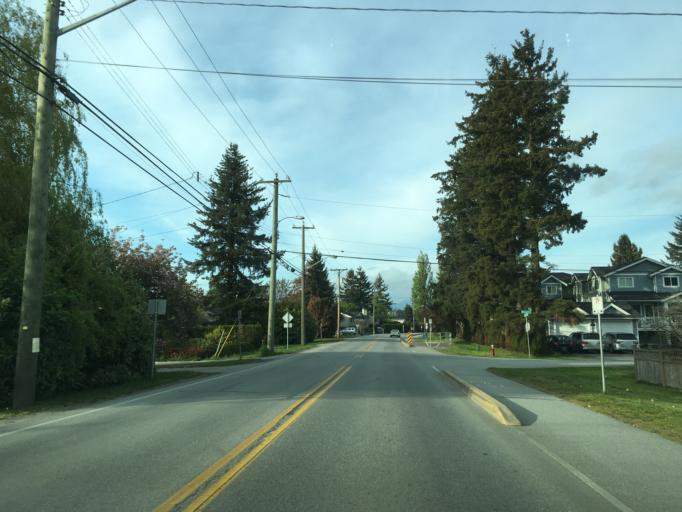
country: CA
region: British Columbia
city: New Westminster
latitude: 49.1793
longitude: -122.9672
